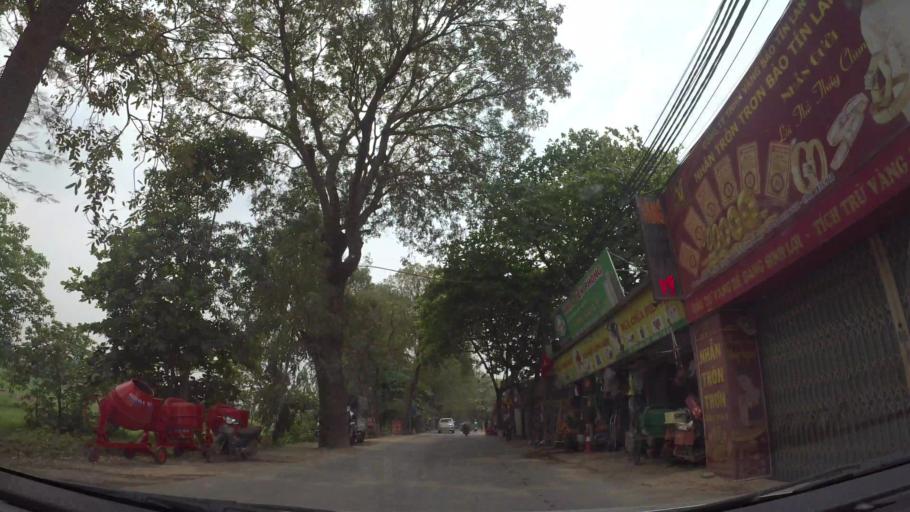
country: VN
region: Ha Noi
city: Cau Dien
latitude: 21.0149
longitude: 105.7457
